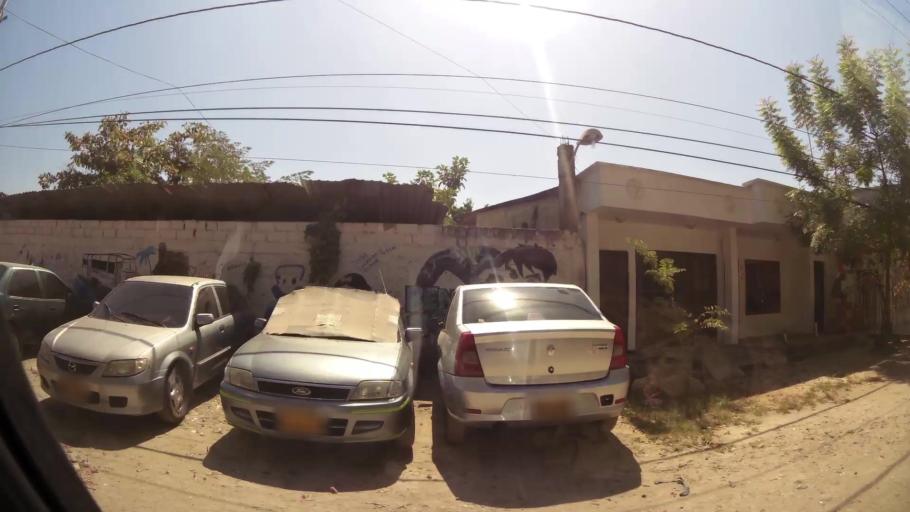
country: CO
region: Bolivar
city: Cartagena
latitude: 10.3834
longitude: -75.4567
